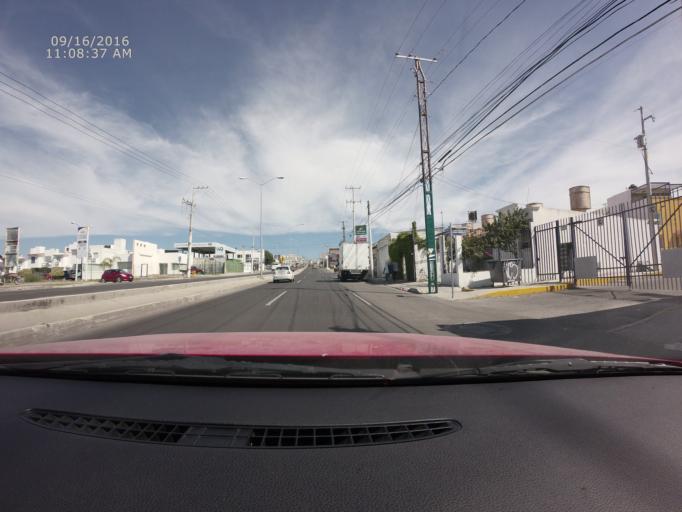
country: MX
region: Queretaro
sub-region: Queretaro
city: Sergio Villasenor
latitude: 20.6332
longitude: -100.4136
